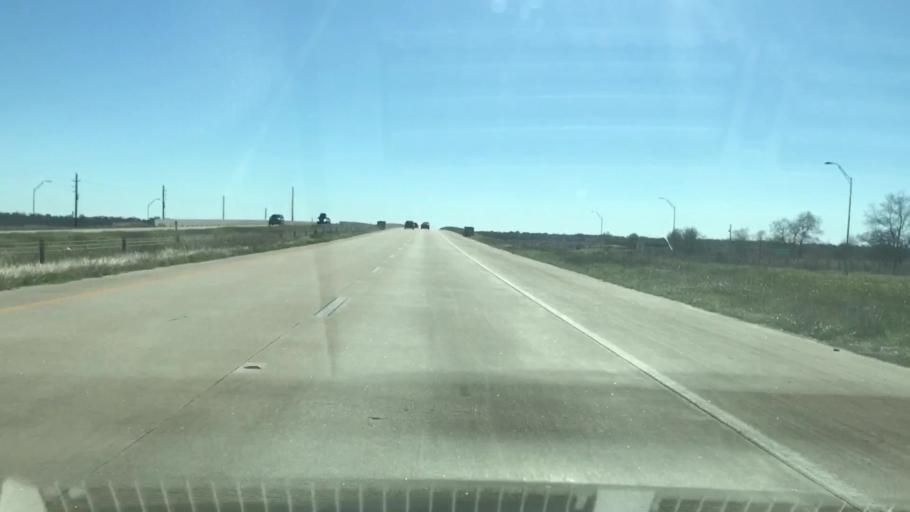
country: US
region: Texas
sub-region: Harris County
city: Cypress
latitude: 29.9809
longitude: -95.7697
